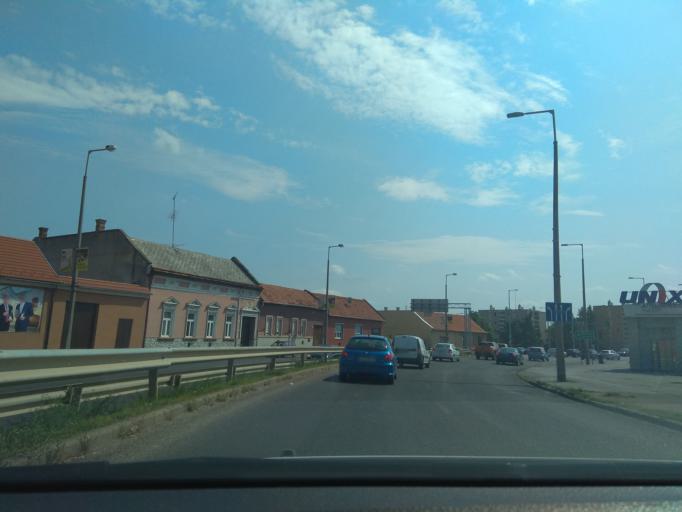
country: HU
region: Heves
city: Eger
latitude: 47.8908
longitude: 20.3795
